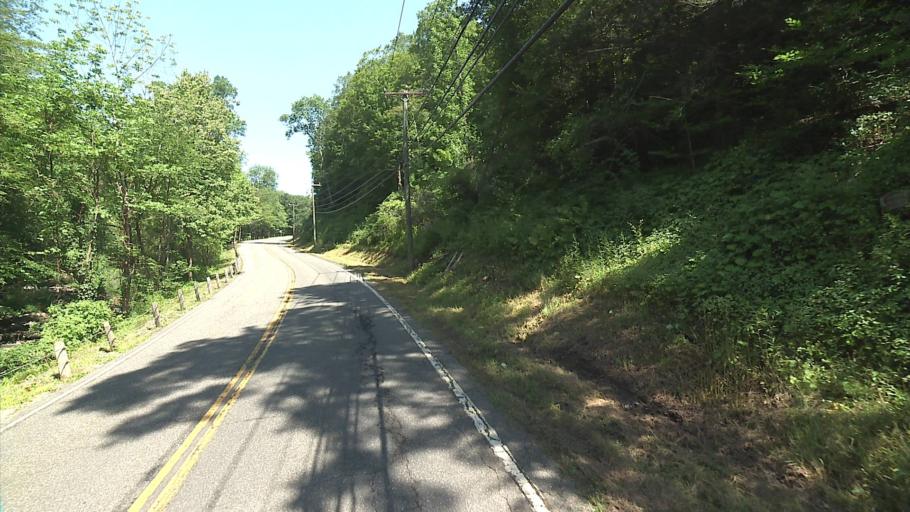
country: US
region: Connecticut
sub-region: Litchfield County
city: New Preston
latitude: 41.7070
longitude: -73.3450
